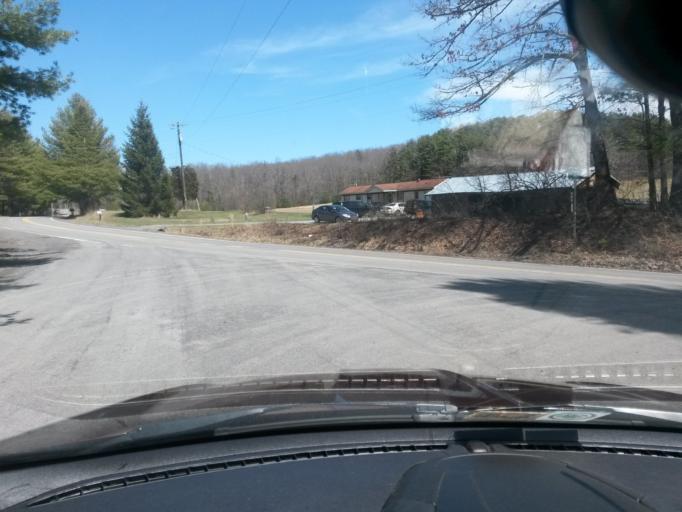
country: US
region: West Virginia
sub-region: Greenbrier County
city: White Sulphur Springs
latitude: 37.6332
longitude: -80.3406
